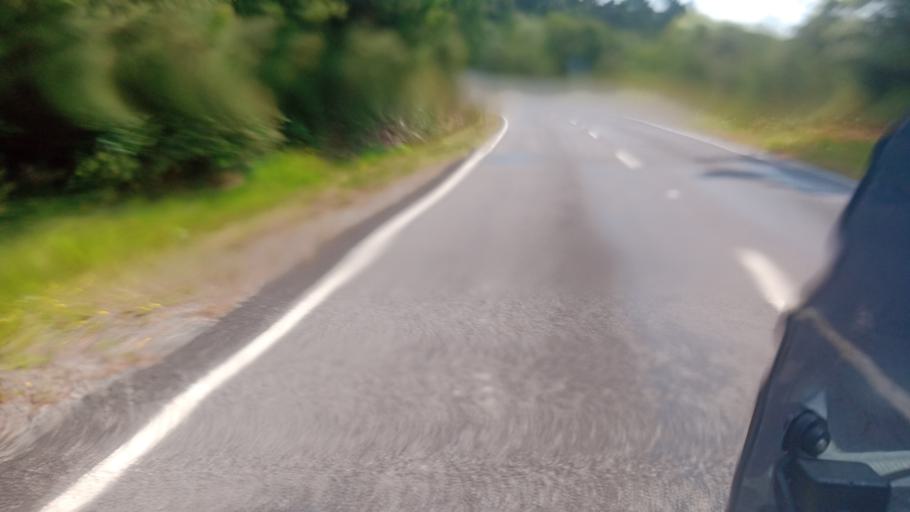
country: NZ
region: Bay of Plenty
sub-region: Opotiki District
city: Opotiki
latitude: -37.5755
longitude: 178.0680
